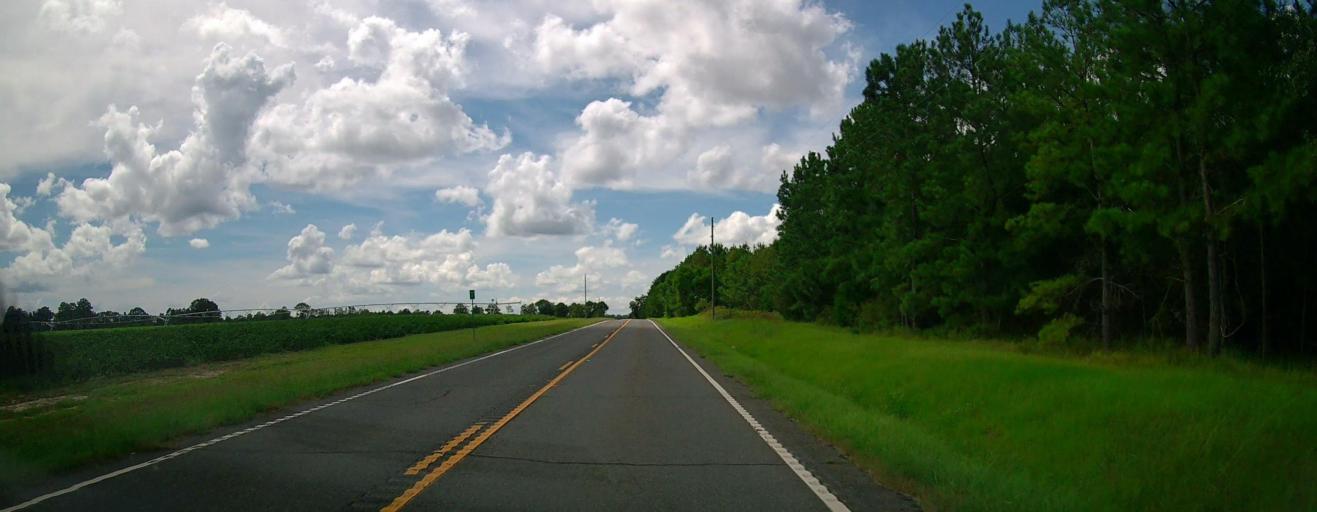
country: US
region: Georgia
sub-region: Macon County
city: Marshallville
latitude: 32.4336
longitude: -84.0606
